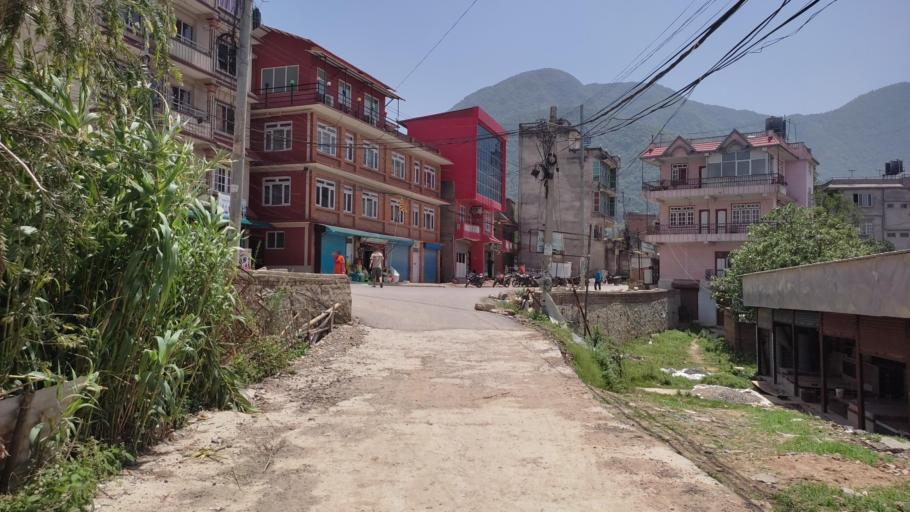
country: NP
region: Central Region
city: Kirtipur
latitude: 27.6675
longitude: 85.2668
